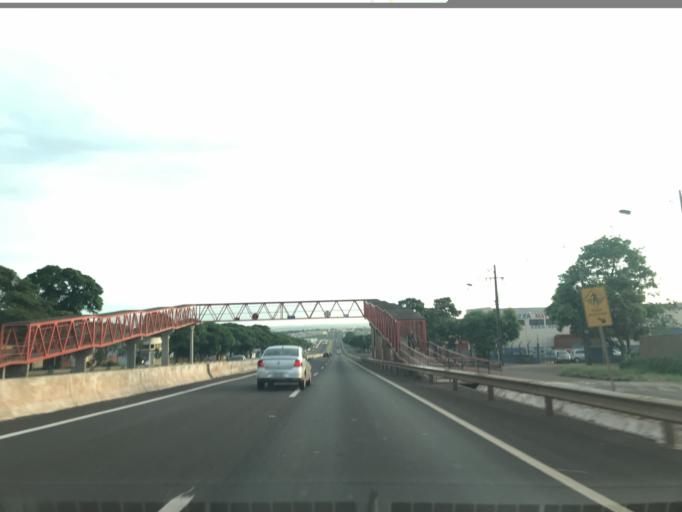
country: BR
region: Parana
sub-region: Maringa
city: Maringa
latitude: -23.4005
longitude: -51.9786
